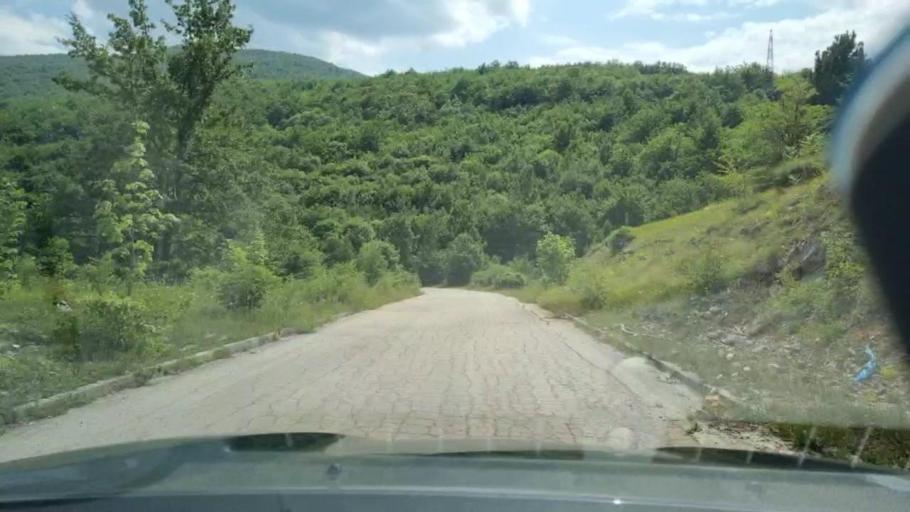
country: BA
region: Federation of Bosnia and Herzegovina
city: Bosansko Grahovo
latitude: 44.2984
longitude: 16.2743
